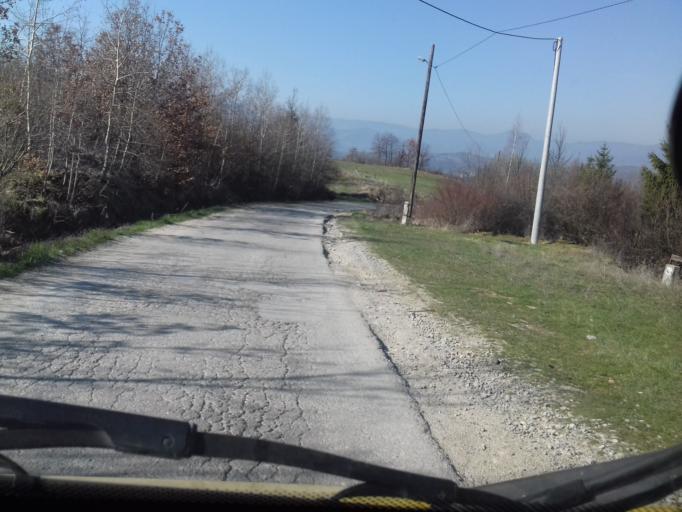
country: BA
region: Federation of Bosnia and Herzegovina
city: Lokvine
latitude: 44.2436
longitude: 17.7921
